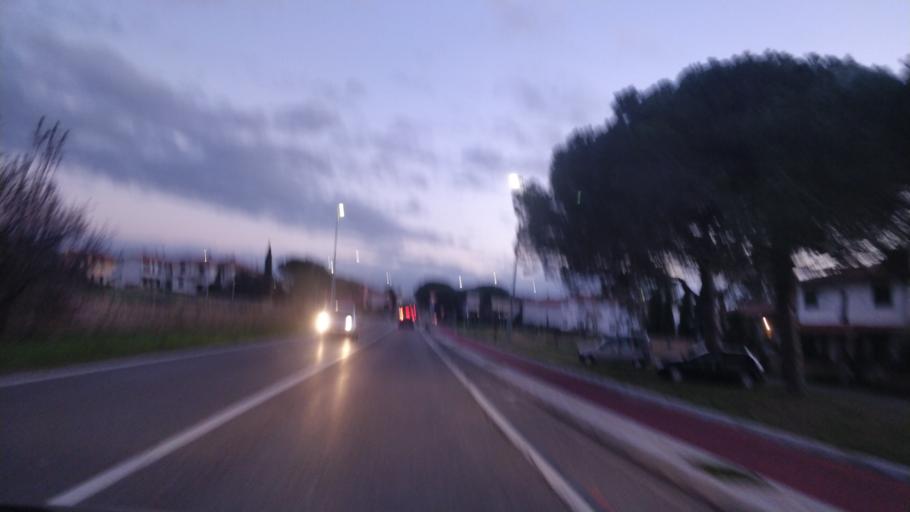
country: IT
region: Tuscany
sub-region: Provincia di Livorno
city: Vada
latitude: 43.3563
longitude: 10.4550
